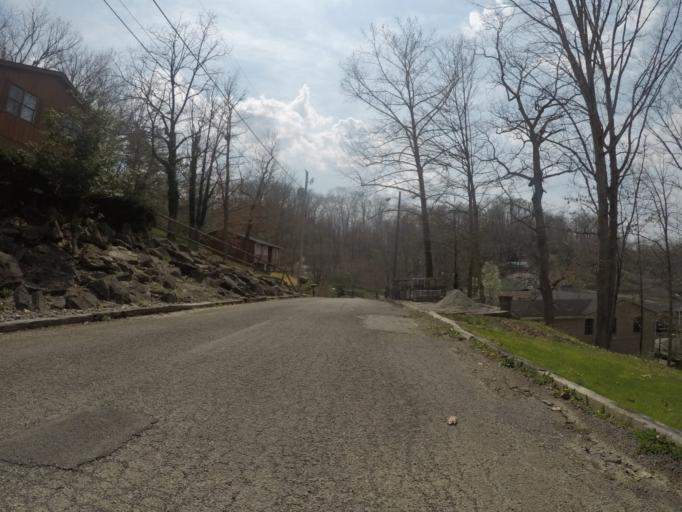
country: US
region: West Virginia
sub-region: Cabell County
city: Pea Ridge
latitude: 38.4023
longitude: -82.3344
